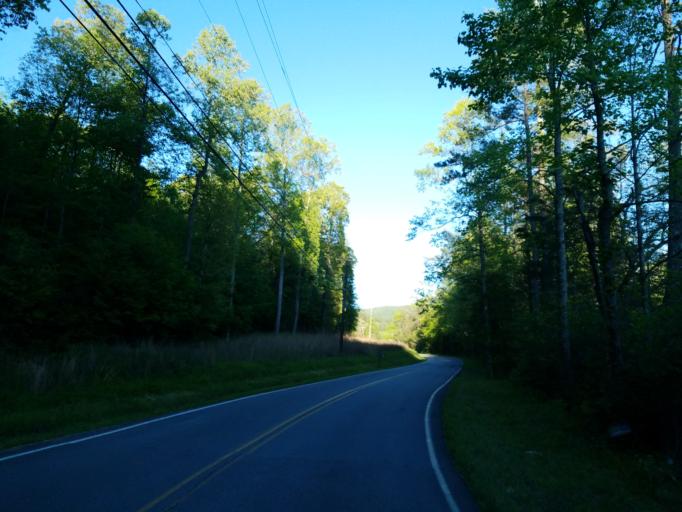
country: US
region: Georgia
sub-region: Fannin County
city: Blue Ridge
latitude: 34.7584
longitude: -84.2034
